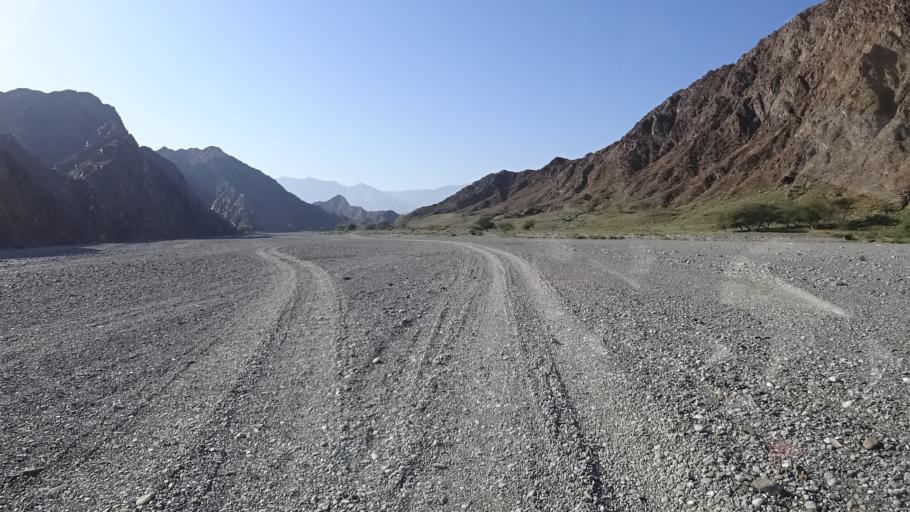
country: OM
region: Al Batinah
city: Bayt al `Awabi
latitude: 23.4059
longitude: 57.6661
